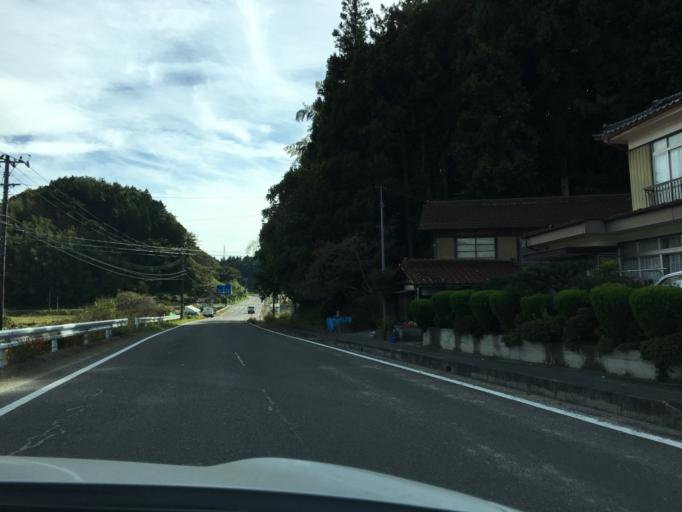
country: JP
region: Fukushima
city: Miharu
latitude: 37.5001
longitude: 140.4995
